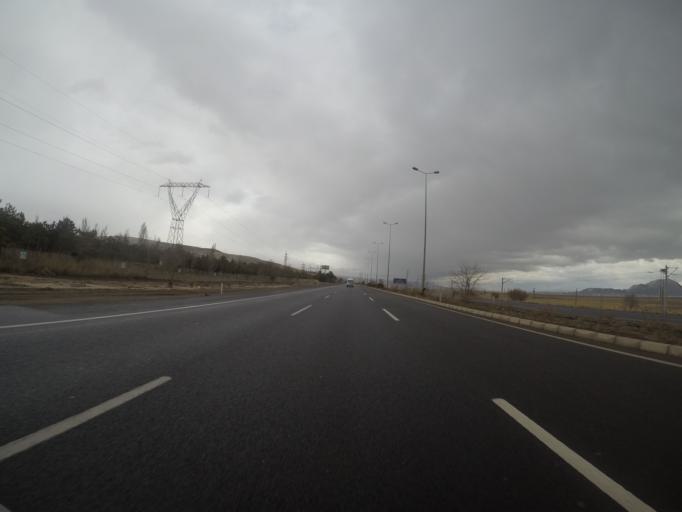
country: TR
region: Kayseri
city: Incesu
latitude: 38.7141
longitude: 35.2659
